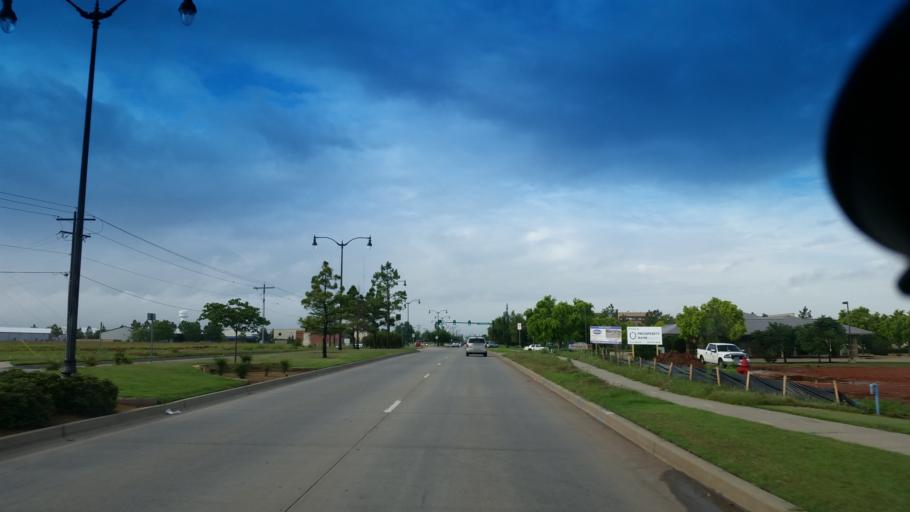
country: US
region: Oklahoma
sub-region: Oklahoma County
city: Edmond
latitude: 35.6351
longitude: -97.4961
